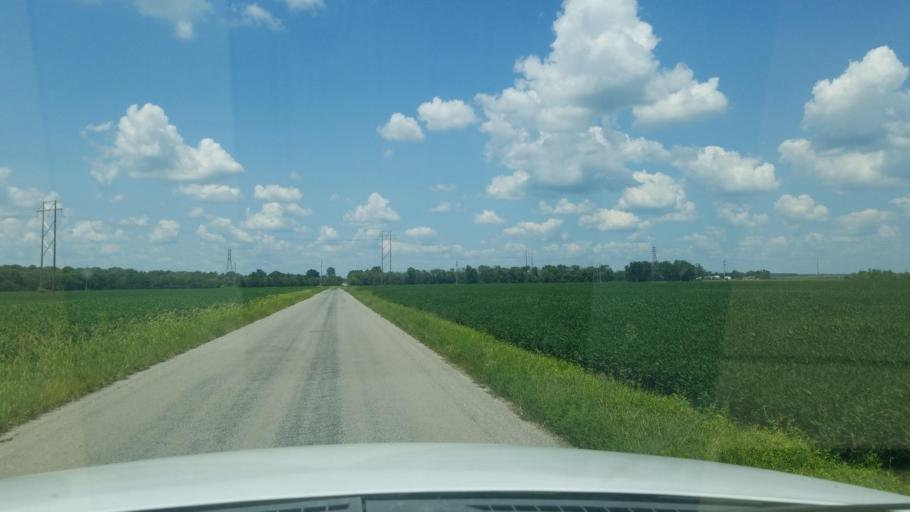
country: US
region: Illinois
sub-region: Saline County
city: Harrisburg
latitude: 37.7719
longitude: -88.5171
